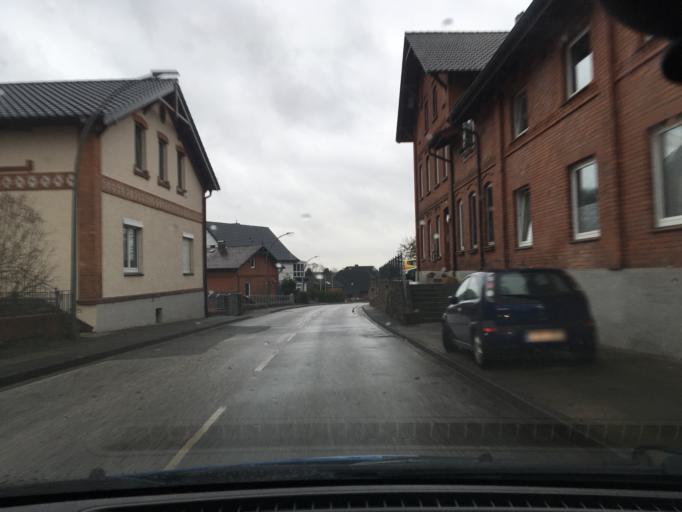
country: DE
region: Lower Saxony
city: Tespe
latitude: 53.4045
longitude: 10.4312
